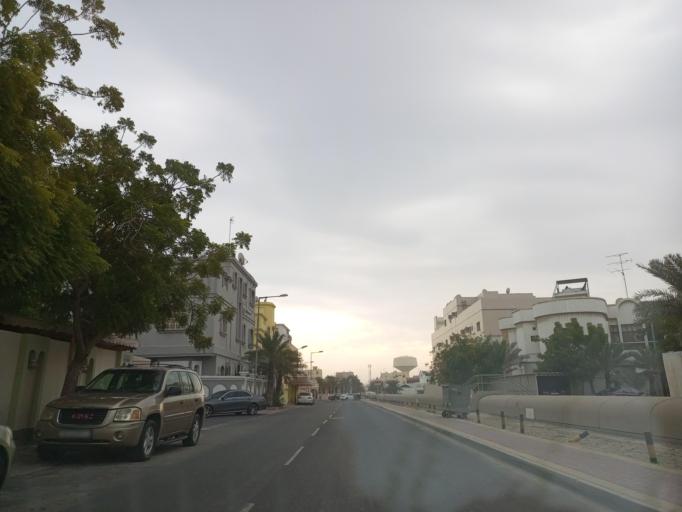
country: BH
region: Muharraq
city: Al Hadd
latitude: 26.2605
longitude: 50.6380
